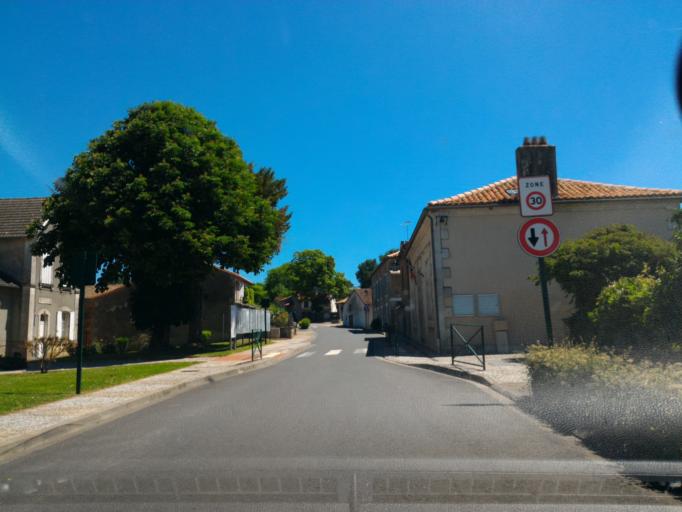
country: FR
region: Poitou-Charentes
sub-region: Departement de la Vienne
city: Availles-Limouzine
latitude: 46.1024
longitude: 0.7050
